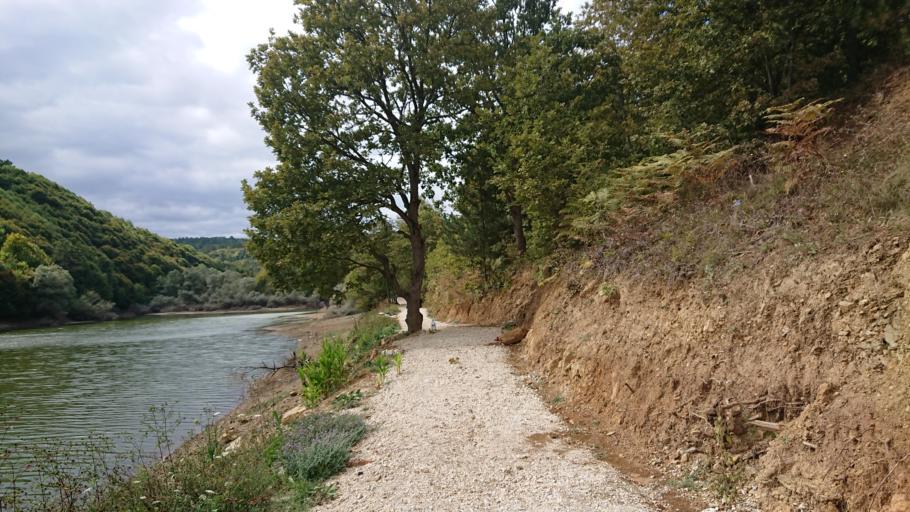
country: TR
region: Bilecik
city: Pazaryeri
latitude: 40.0175
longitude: 29.7929
